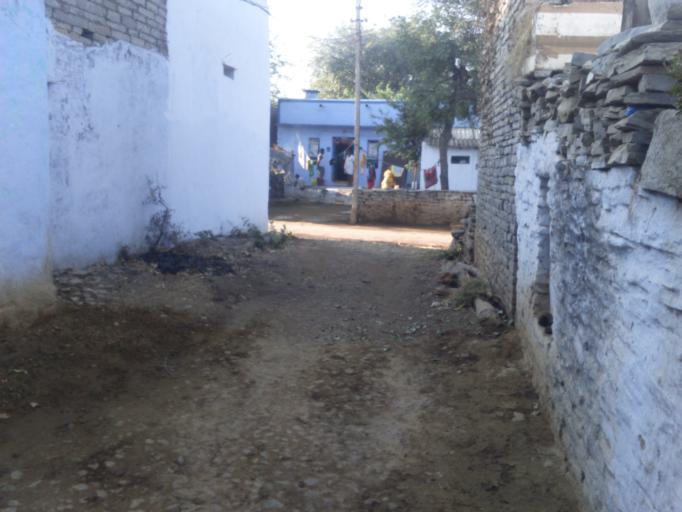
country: IN
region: Andhra Pradesh
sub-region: Kurnool
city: Nandikotkur
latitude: 15.9656
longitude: 78.2806
